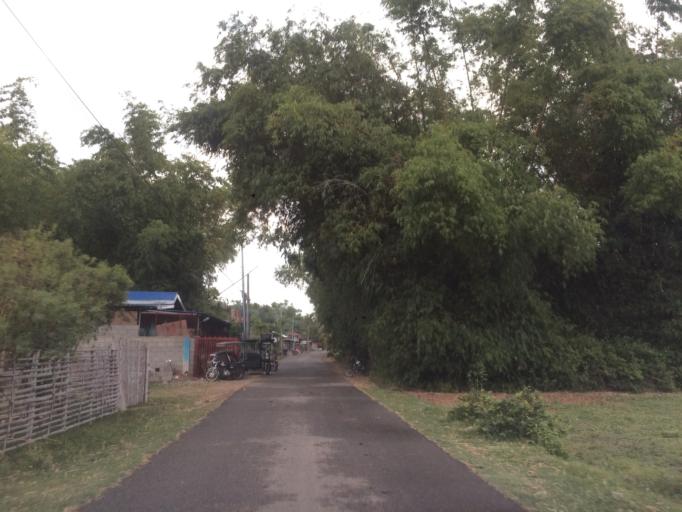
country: PH
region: Ilocos
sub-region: Province of Pangasinan
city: Anambongan
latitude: 15.8713
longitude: 120.3876
